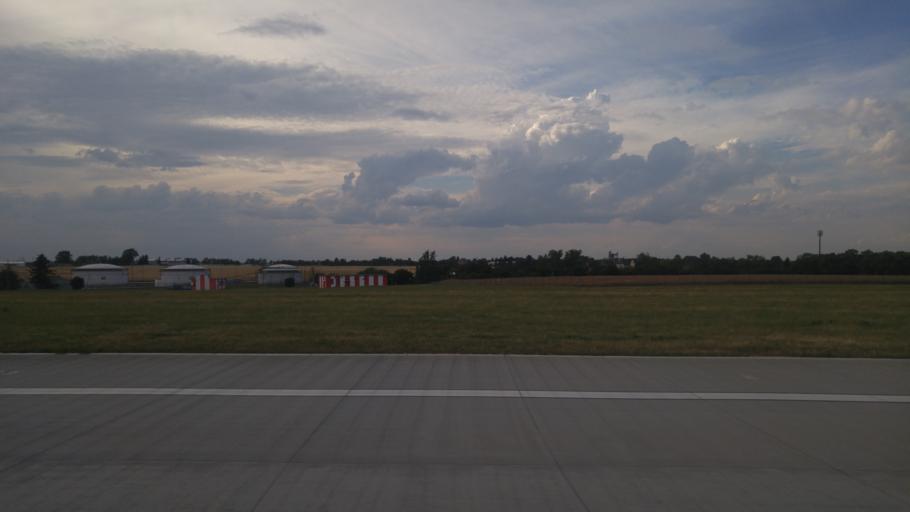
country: CZ
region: Central Bohemia
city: Hostivice
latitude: 50.1121
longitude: 14.2604
